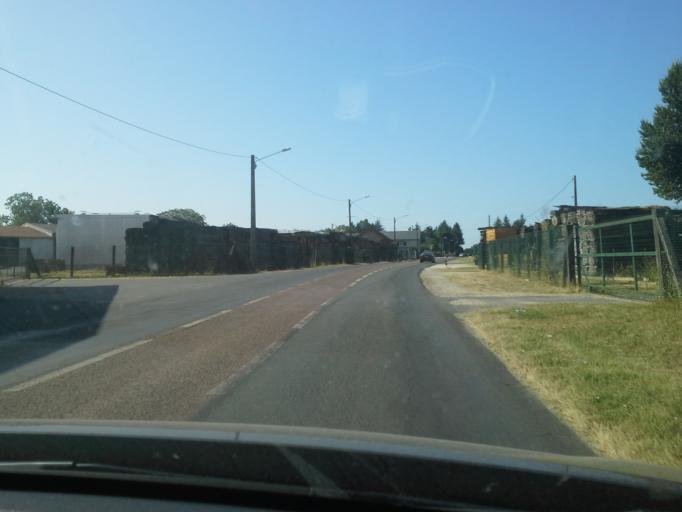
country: FR
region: Centre
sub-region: Departement du Loir-et-Cher
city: Chailles
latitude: 47.5203
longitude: 1.3009
